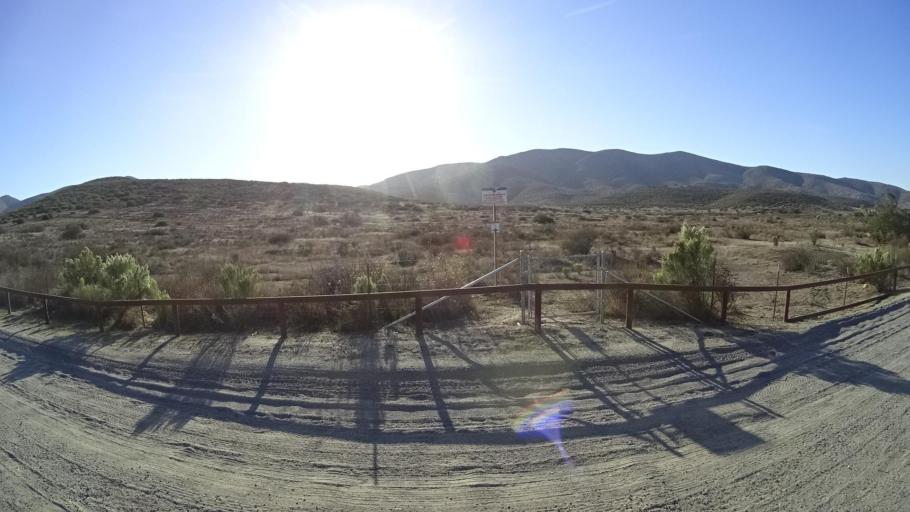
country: US
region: California
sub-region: San Diego County
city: Jamul
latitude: 32.6756
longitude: -116.9201
